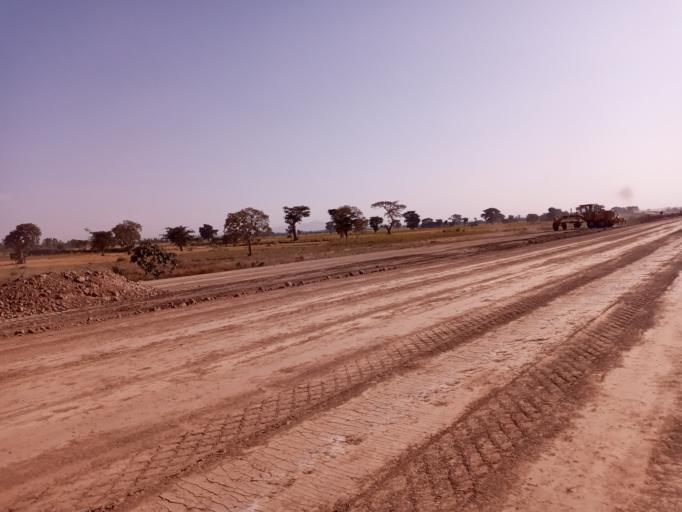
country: ET
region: Oromiya
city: Shashemene
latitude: 7.3047
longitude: 38.6185
